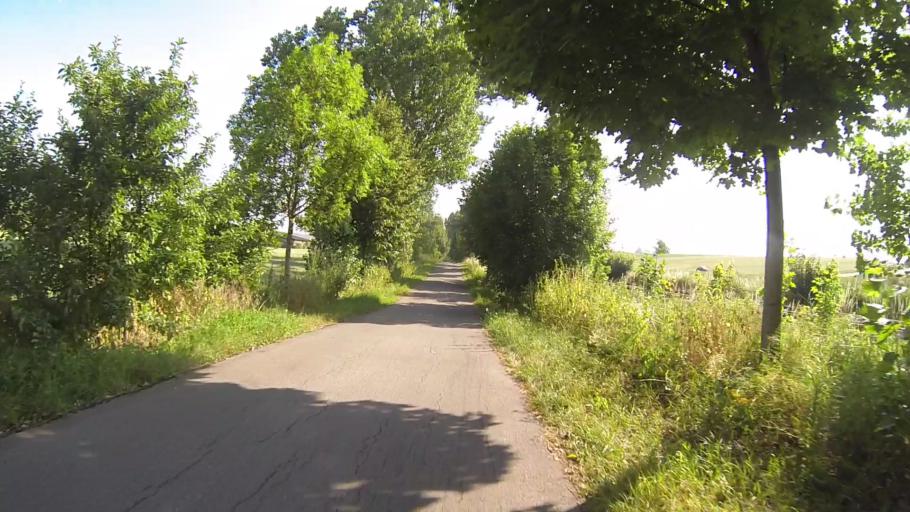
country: DE
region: Baden-Wuerttemberg
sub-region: Tuebingen Region
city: Erbach
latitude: 48.3449
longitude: 9.9146
